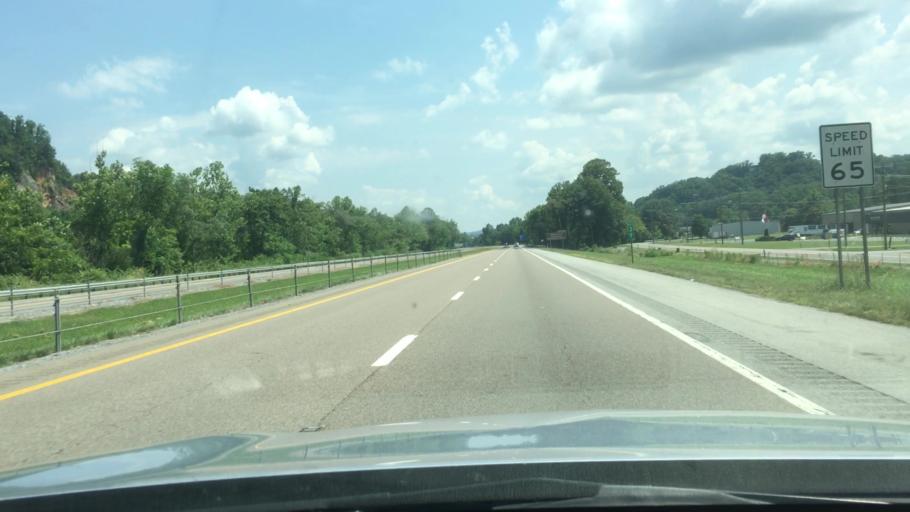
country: US
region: Tennessee
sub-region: Unicoi County
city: Banner Hill
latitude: 36.1312
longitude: -82.4378
